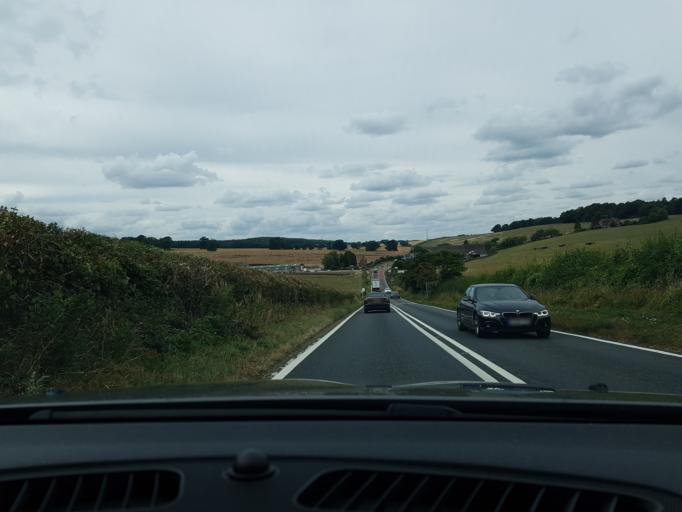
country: GB
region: England
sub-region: Hampshire
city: Kingsclere
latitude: 51.2985
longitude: -1.1819
